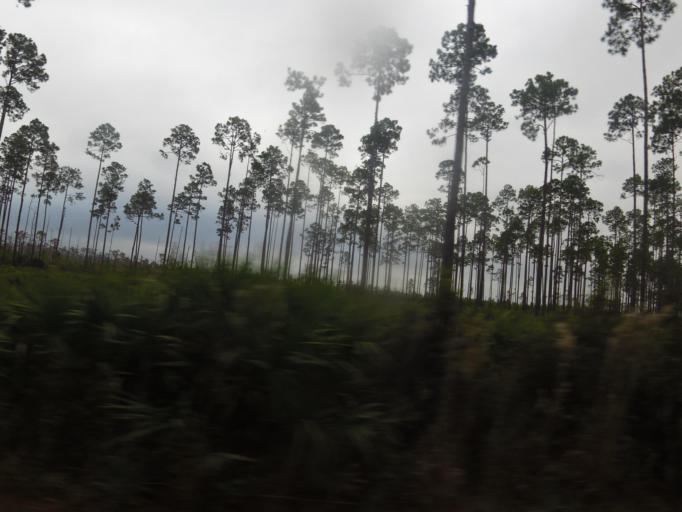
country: US
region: Georgia
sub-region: Charlton County
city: Folkston
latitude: 30.7087
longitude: -82.1580
